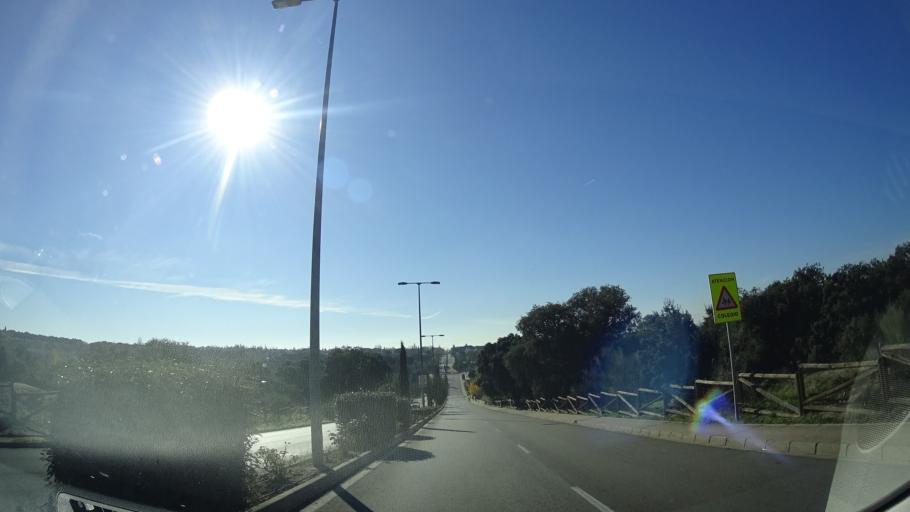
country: ES
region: Madrid
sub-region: Provincia de Madrid
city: Las Matas
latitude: 40.5280
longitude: -3.9150
